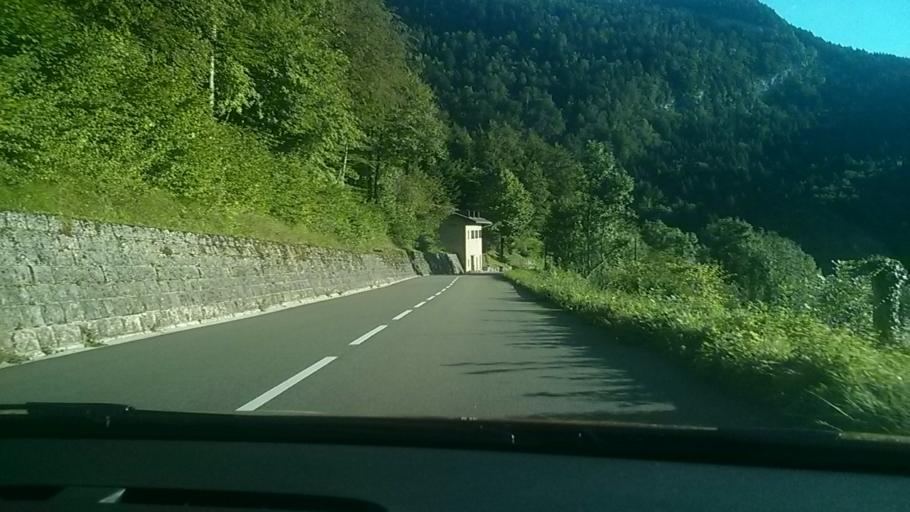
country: FR
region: Franche-Comte
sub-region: Departement du Jura
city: Saint-Claude
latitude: 46.3573
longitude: 5.9081
